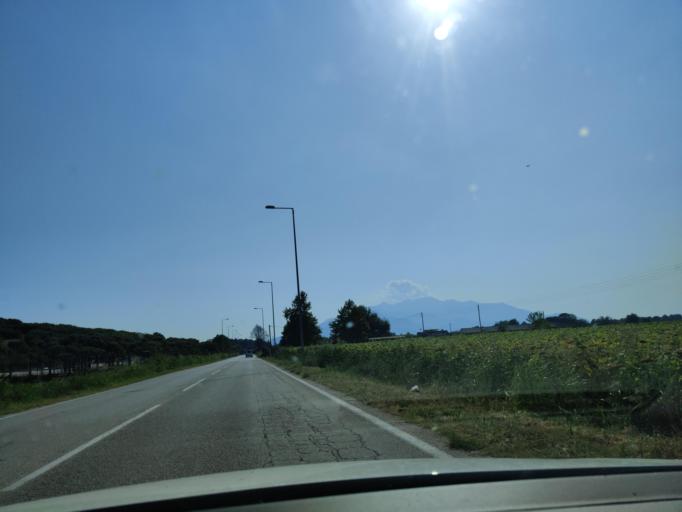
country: GR
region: East Macedonia and Thrace
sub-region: Nomos Kavalas
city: Amygdaleonas
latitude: 40.9744
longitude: 24.3591
